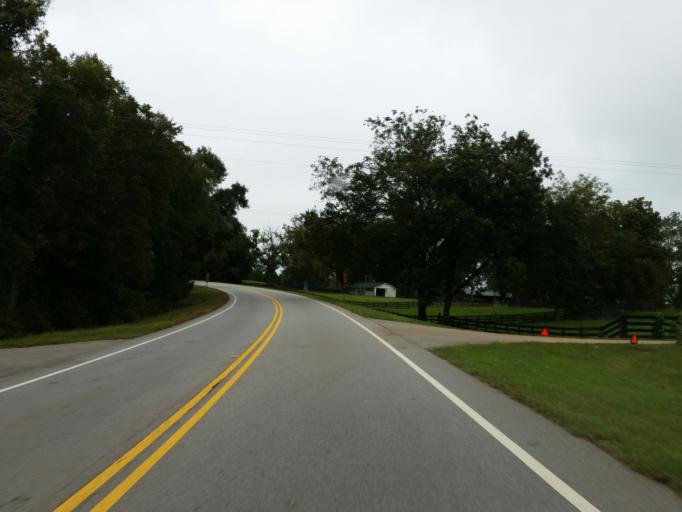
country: US
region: Georgia
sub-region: Lamar County
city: Barnesville
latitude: 32.9576
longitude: -84.1097
